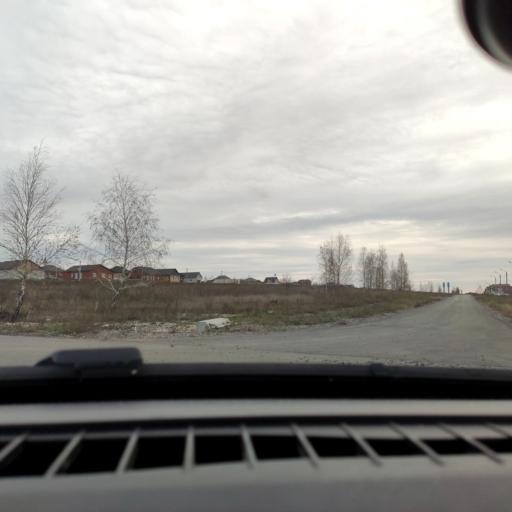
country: RU
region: Belgorod
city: Ilovka
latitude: 50.6497
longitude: 38.6218
